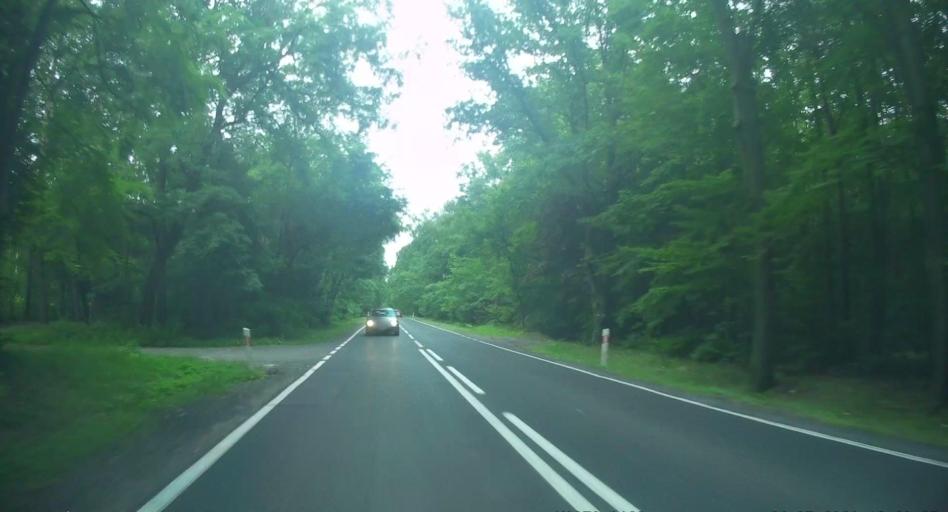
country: PL
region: Lodz Voivodeship
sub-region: Powiat tomaszowski
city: Lubochnia
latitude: 51.5438
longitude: 20.1088
